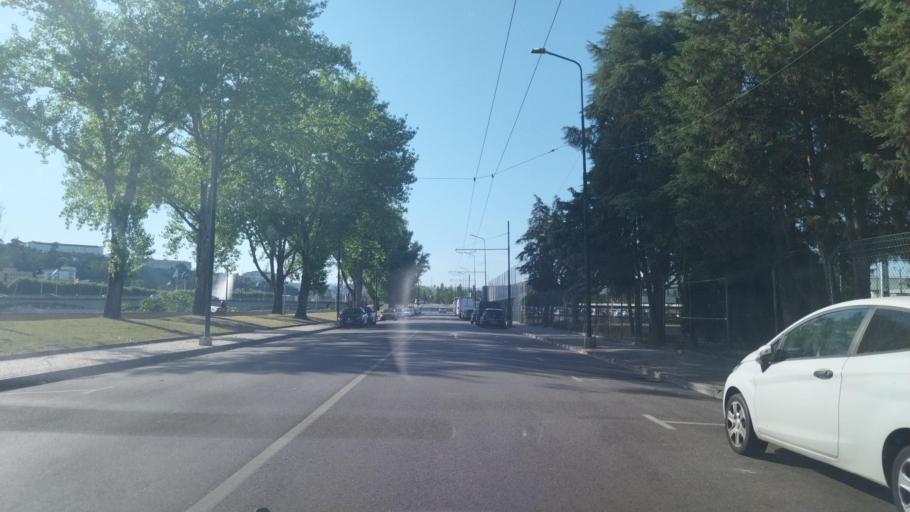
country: PT
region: Coimbra
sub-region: Coimbra
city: Coimbra
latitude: 40.2068
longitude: -8.4335
